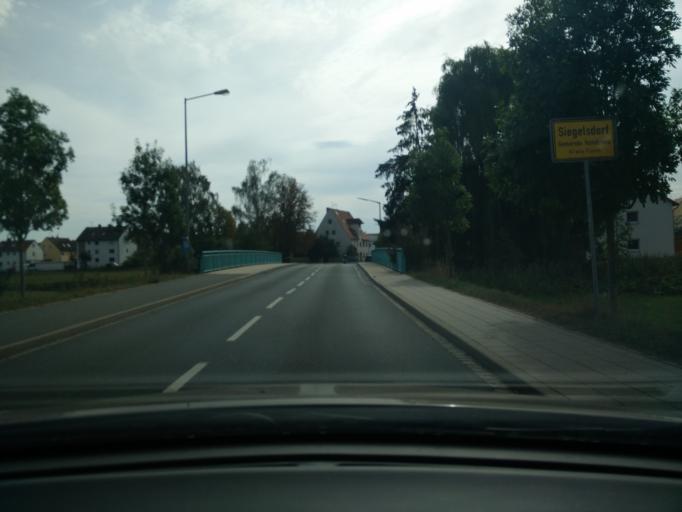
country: DE
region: Bavaria
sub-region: Regierungsbezirk Mittelfranken
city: Veitsbronn
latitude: 49.5106
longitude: 10.8796
